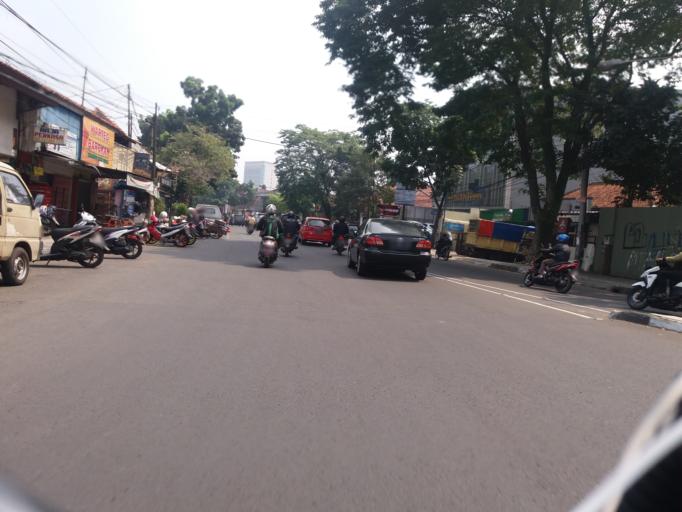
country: ID
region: West Java
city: Bandung
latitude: -6.9078
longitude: 107.6075
